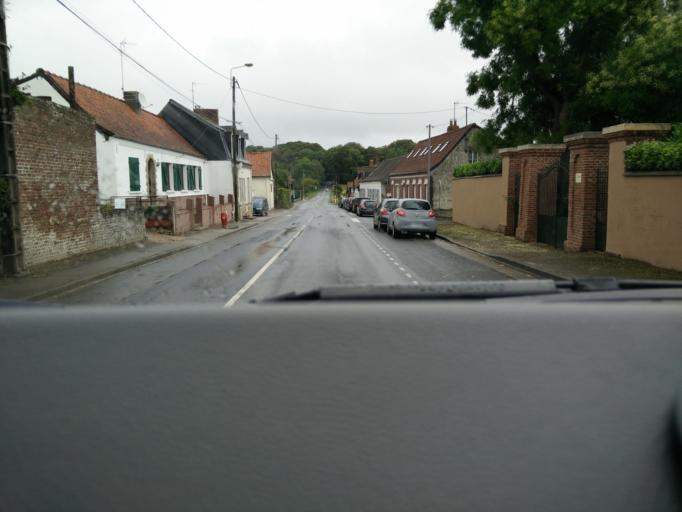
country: FR
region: Picardie
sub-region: Departement de la Somme
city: Rue
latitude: 50.2785
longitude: 1.7206
